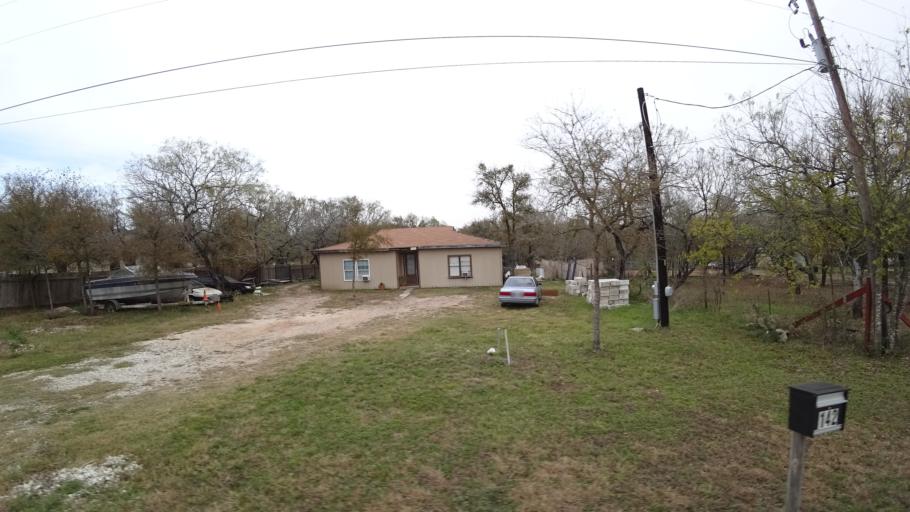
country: US
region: Texas
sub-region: Travis County
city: Garfield
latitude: 30.1016
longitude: -97.5722
